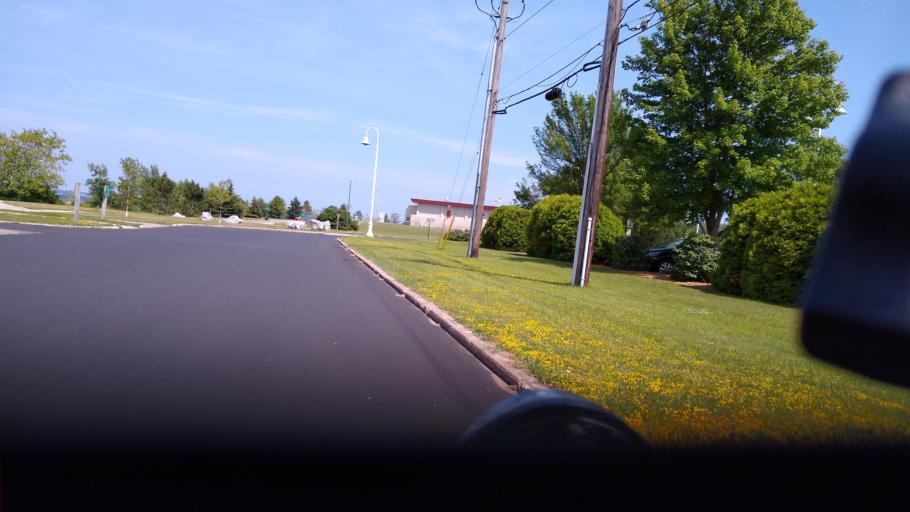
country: US
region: Michigan
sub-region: Delta County
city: Escanaba
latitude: 45.7444
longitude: -87.0435
